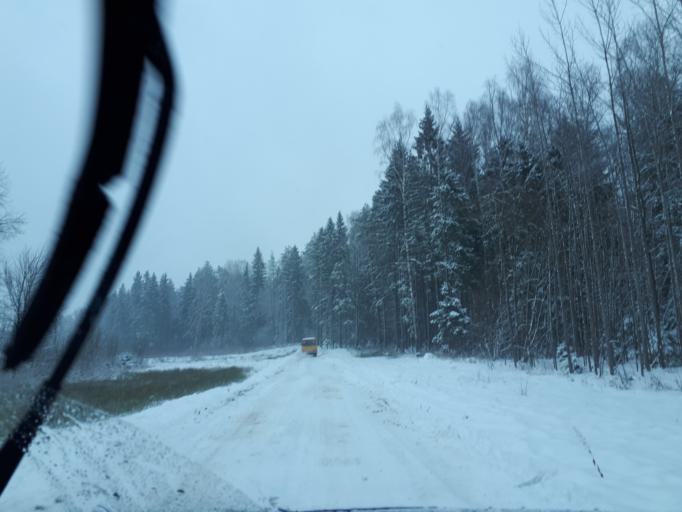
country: BY
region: Vitebsk
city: Vitebsk
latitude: 55.2630
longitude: 30.2081
